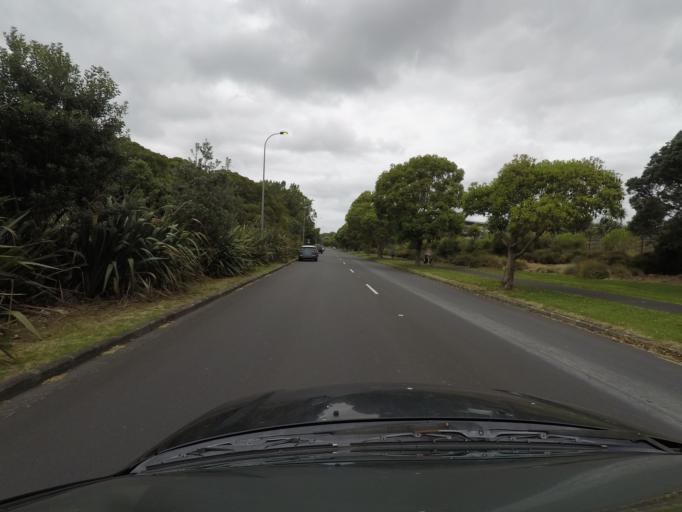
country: NZ
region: Auckland
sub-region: Auckland
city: Rosebank
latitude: -36.8605
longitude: 174.7120
